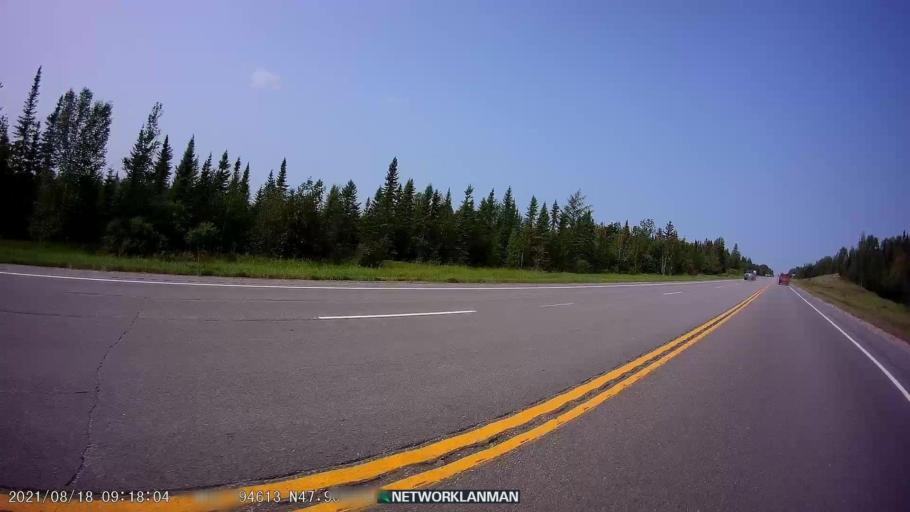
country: US
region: Minnesota
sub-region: Saint Louis County
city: Mountain Iron
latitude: 47.9057
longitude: -92.7948
